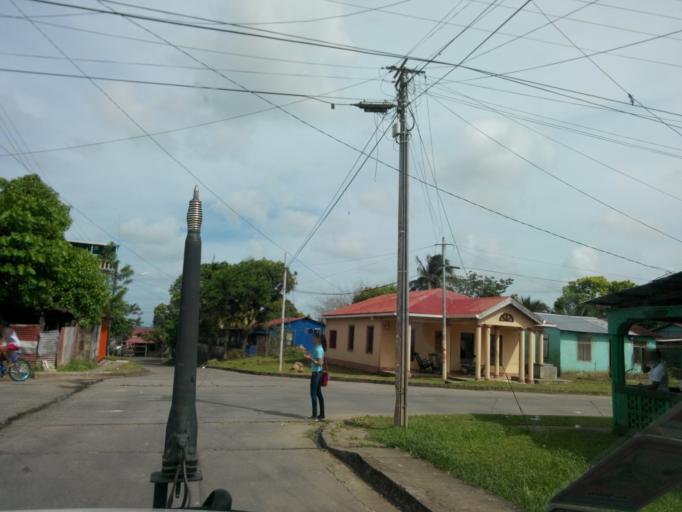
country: NI
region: Atlantico Sur
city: Bluefields
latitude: 11.9988
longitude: -83.7683
